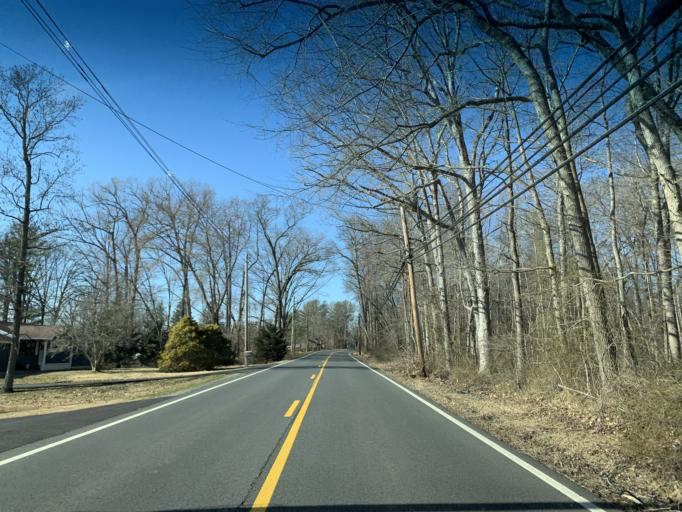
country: US
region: Maryland
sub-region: Cecil County
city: Elkton
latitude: 39.6340
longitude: -75.8621
